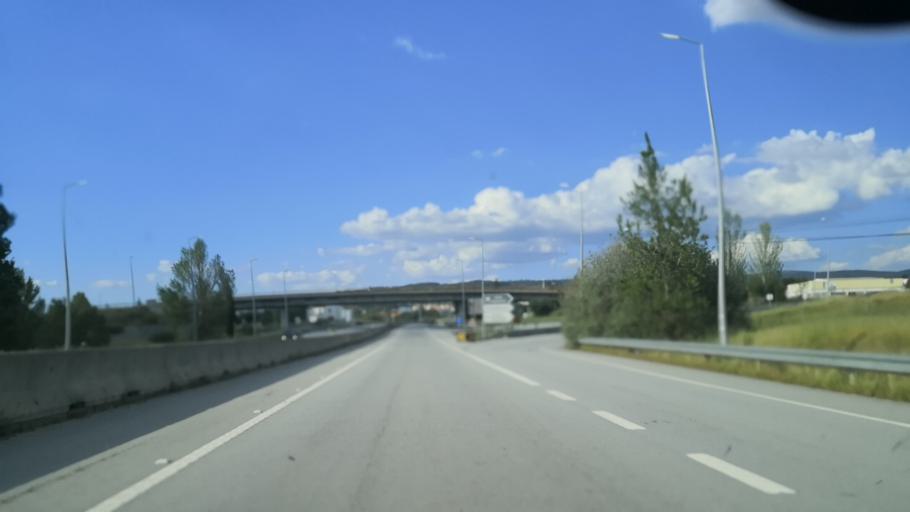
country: PT
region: Portalegre
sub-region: Portalegre
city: Portalegre
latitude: 39.2676
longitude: -7.4412
